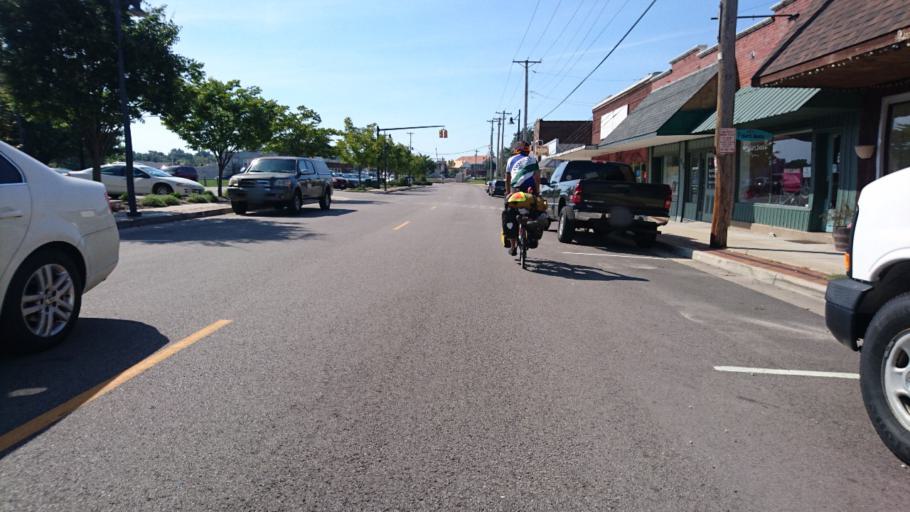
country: US
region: Missouri
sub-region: Franklin County
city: Saint Clair
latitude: 38.3473
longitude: -90.9809
